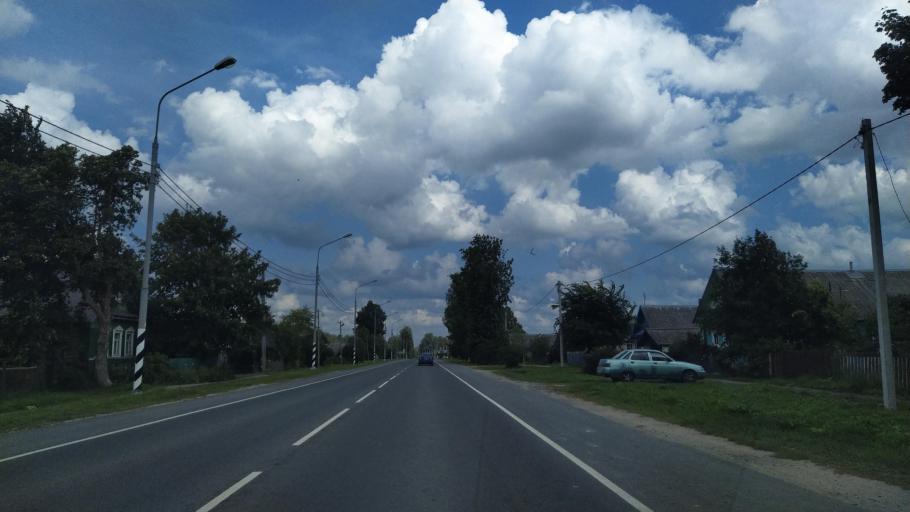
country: RU
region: Novgorod
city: Sol'tsy
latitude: 58.0817
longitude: 30.0983
